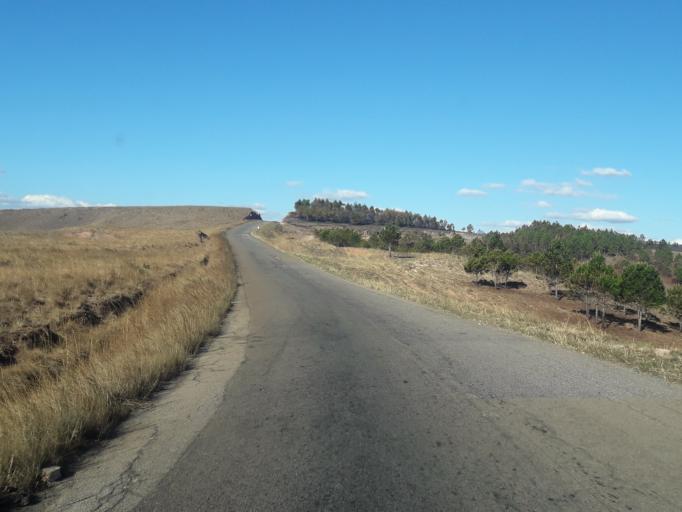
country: MG
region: Analamanga
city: Ankazobe
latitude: -17.8794
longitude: 47.0419
